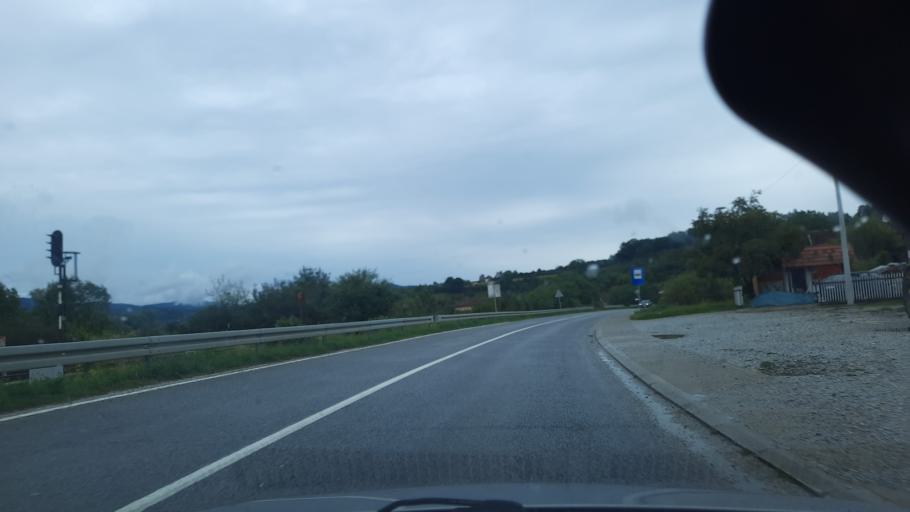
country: RS
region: Central Serbia
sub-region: Sumadijski Okrug
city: Knic
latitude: 43.8361
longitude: 20.7748
